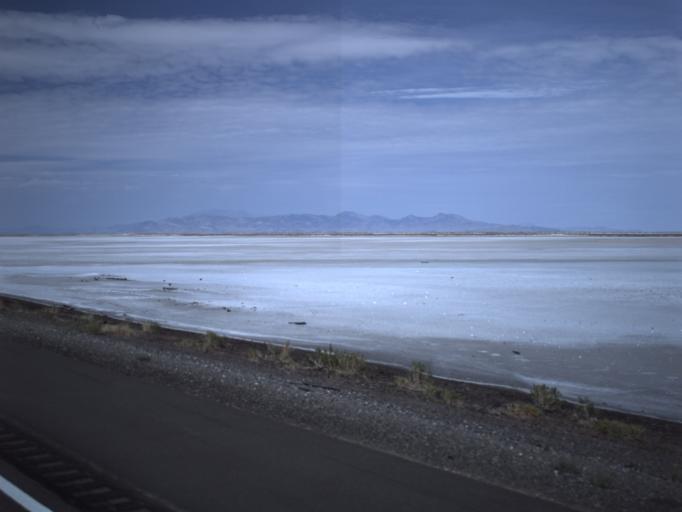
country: US
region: Utah
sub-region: Tooele County
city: Wendover
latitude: 40.7302
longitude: -113.4320
